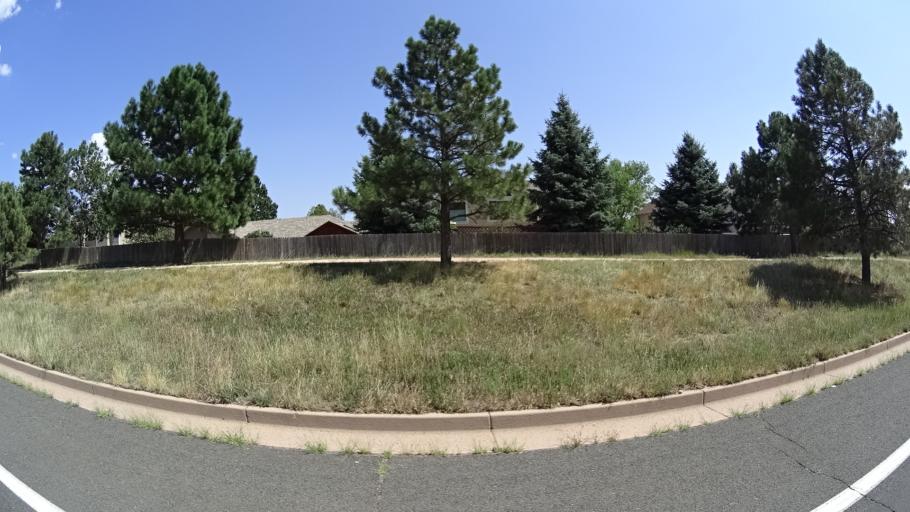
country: US
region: Colorado
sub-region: El Paso County
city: Air Force Academy
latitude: 38.9253
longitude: -104.8669
